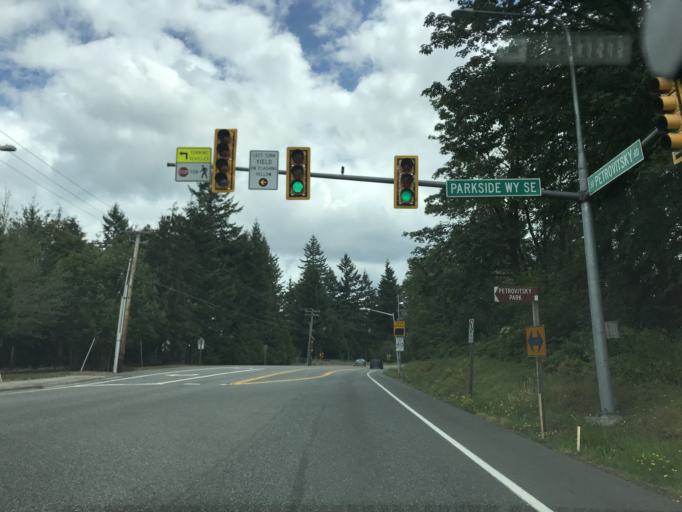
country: US
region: Washington
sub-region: King County
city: Maple Heights-Lake Desire
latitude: 47.4395
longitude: -122.1210
